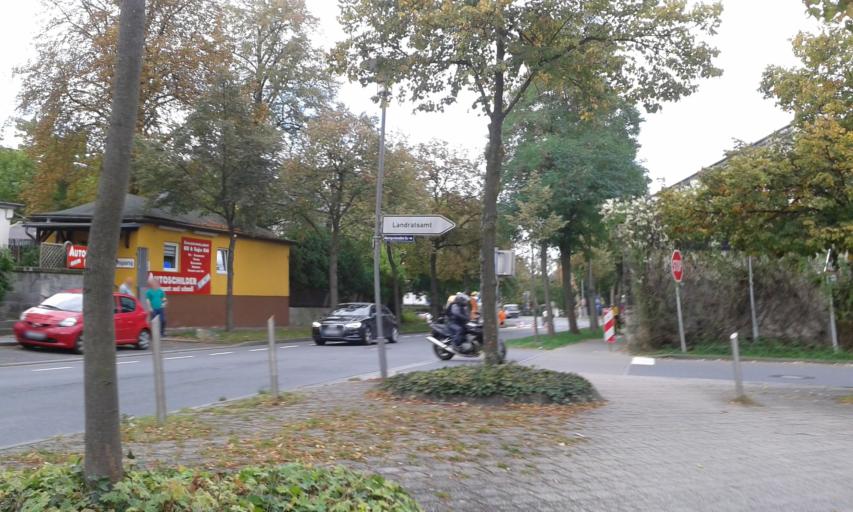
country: DE
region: Bavaria
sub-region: Upper Franconia
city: Bayreuth
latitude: 49.9506
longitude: 11.5830
